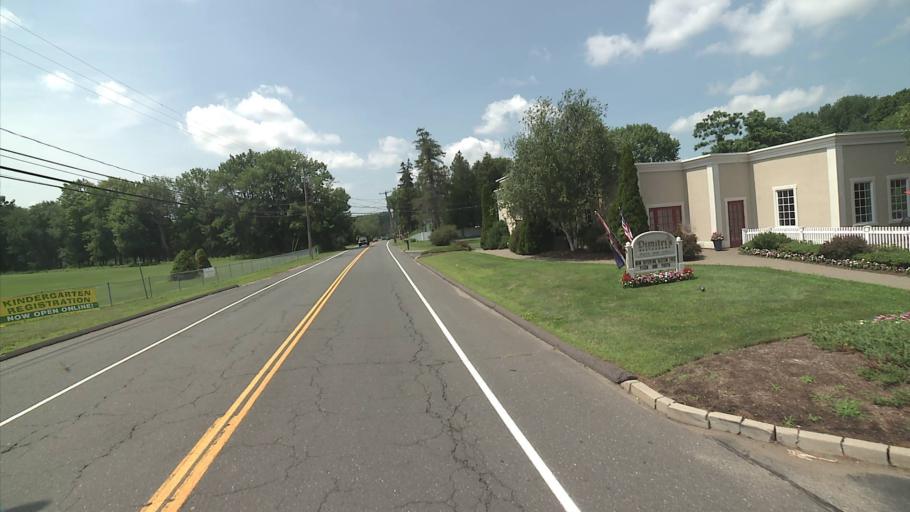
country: US
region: Connecticut
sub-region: Tolland County
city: Coventry Lake
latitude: 41.7957
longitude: -72.3665
